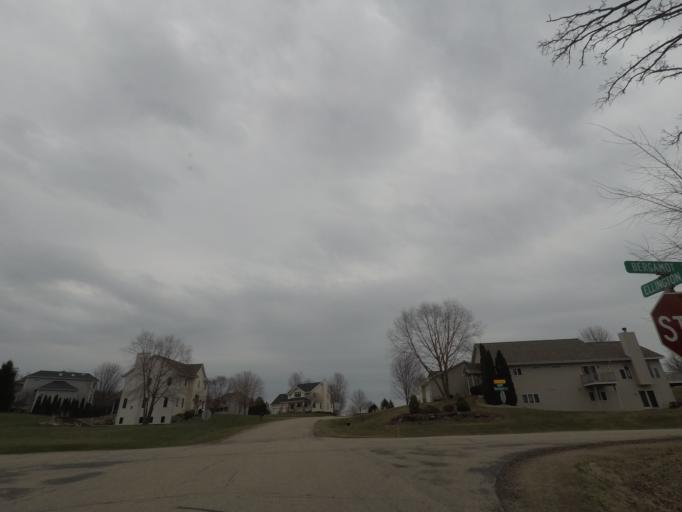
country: US
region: Wisconsin
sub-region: Dane County
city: Middleton
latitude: 43.1147
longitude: -89.5661
